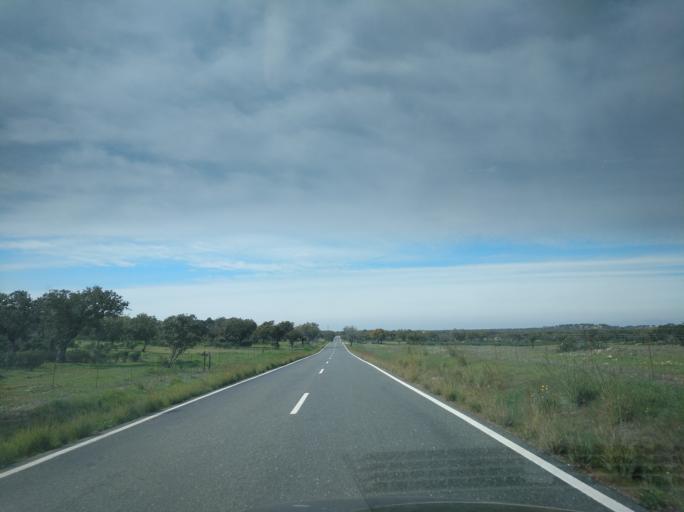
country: PT
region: Beja
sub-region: Mertola
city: Mertola
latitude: 37.7373
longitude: -7.7759
